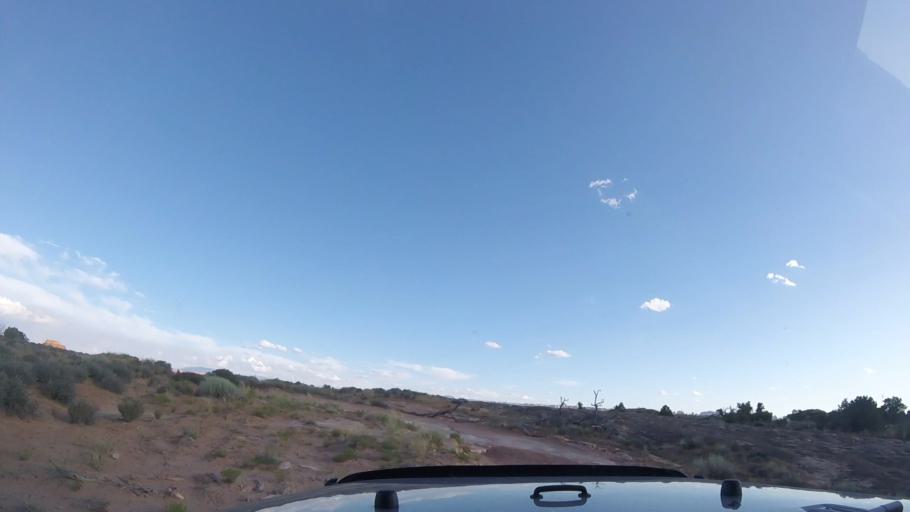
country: US
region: Utah
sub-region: Grand County
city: Moab
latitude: 38.2000
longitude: -109.7825
